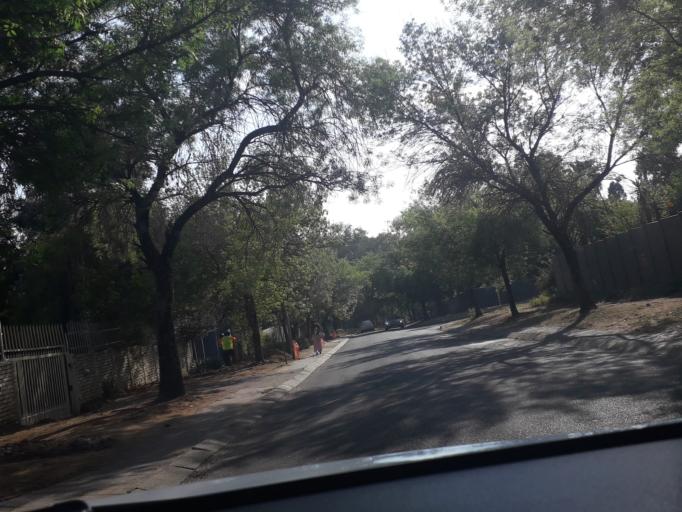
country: ZA
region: Gauteng
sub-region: City of Johannesburg Metropolitan Municipality
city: Diepsloot
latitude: -26.0444
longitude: 27.9835
